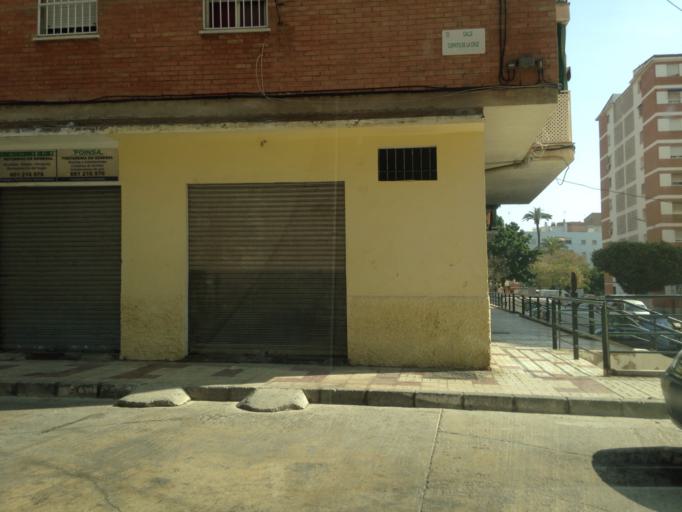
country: ES
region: Andalusia
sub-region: Provincia de Malaga
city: Malaga
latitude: 36.6975
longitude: -4.4524
